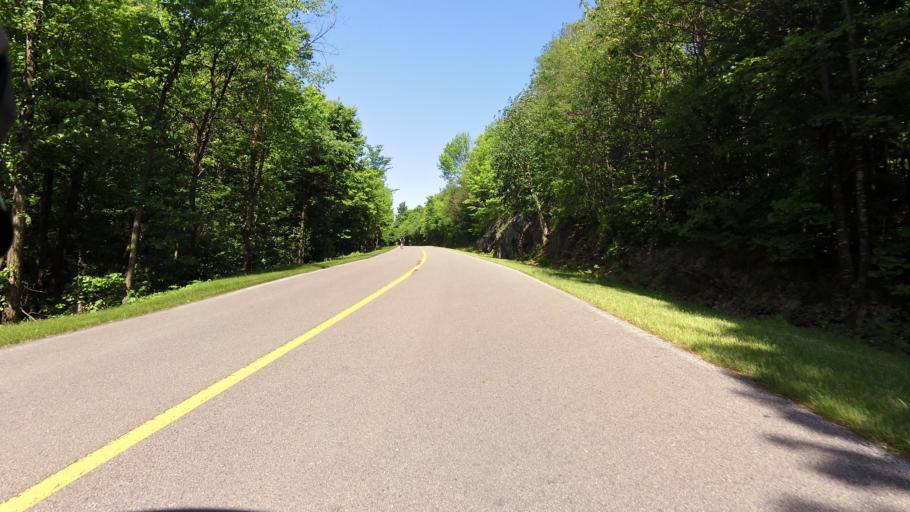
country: CA
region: Quebec
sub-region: Outaouais
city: Wakefield
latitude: 45.5026
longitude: -75.8786
